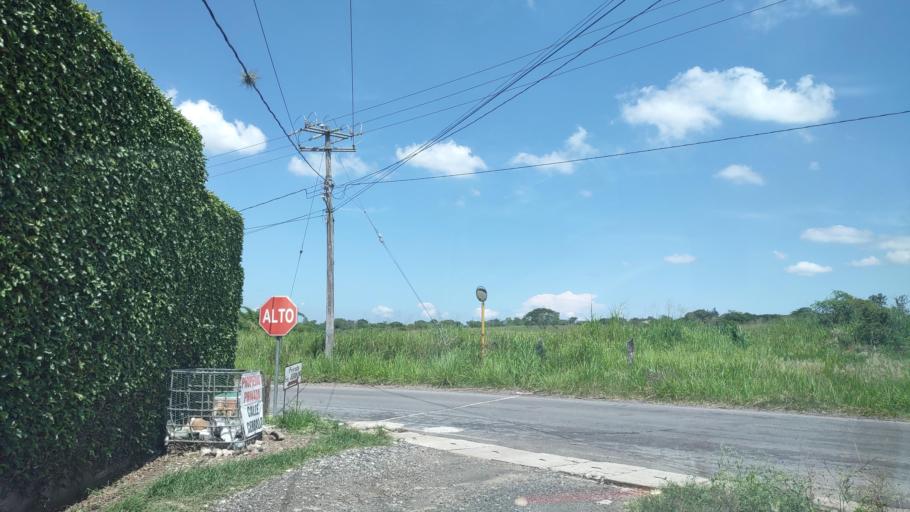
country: MX
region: Veracruz
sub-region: Emiliano Zapata
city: Dos Rios
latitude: 19.4946
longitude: -96.8051
